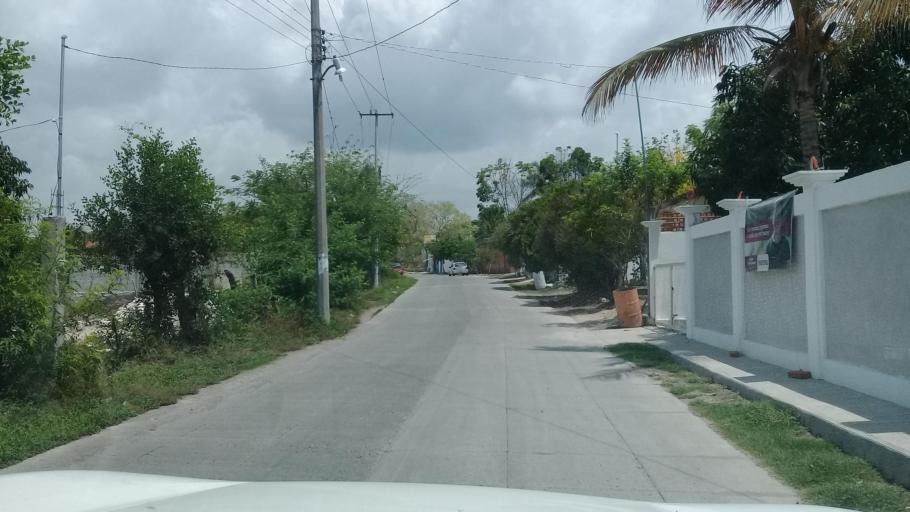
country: MX
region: Veracruz
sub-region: Emiliano Zapata
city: Plan del Rio
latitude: 19.3539
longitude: -96.6472
